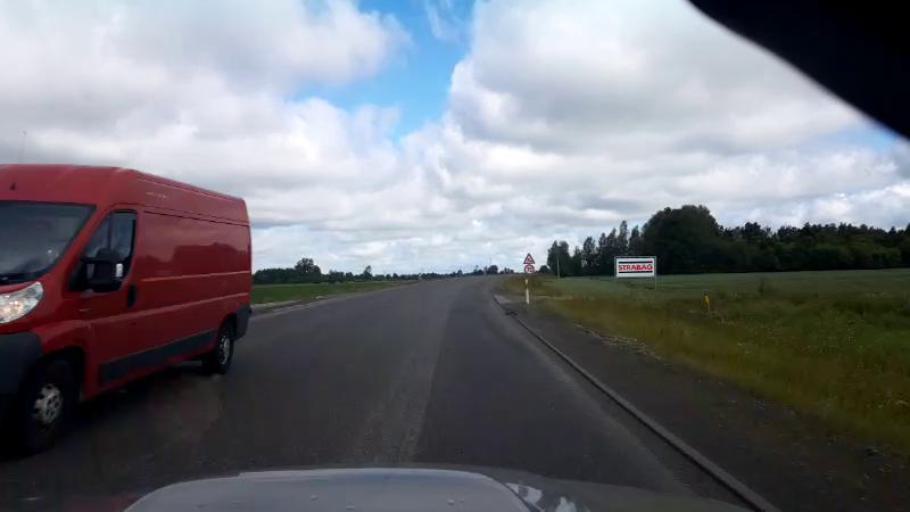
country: LV
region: Bauskas Rajons
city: Bauska
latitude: 56.2980
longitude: 24.3450
